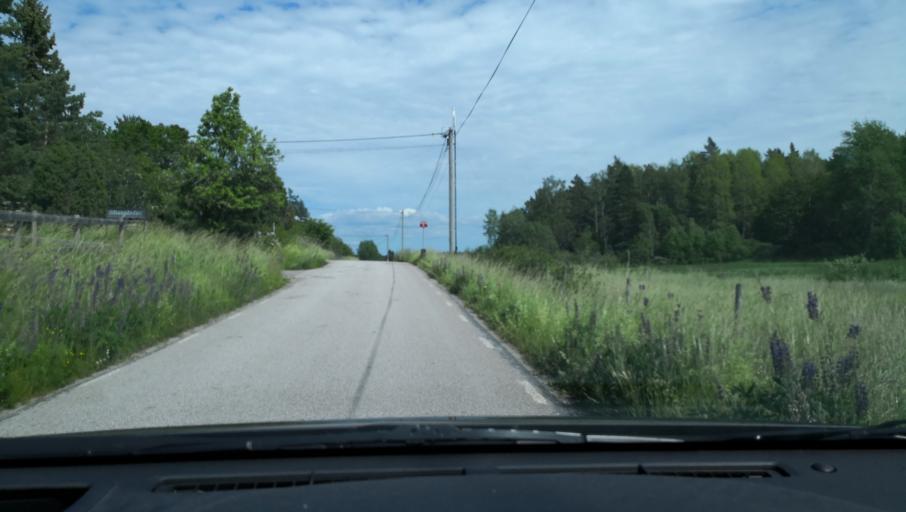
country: SE
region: Uppsala
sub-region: Uppsala Kommun
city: Alsike
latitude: 59.7036
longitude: 17.7094
